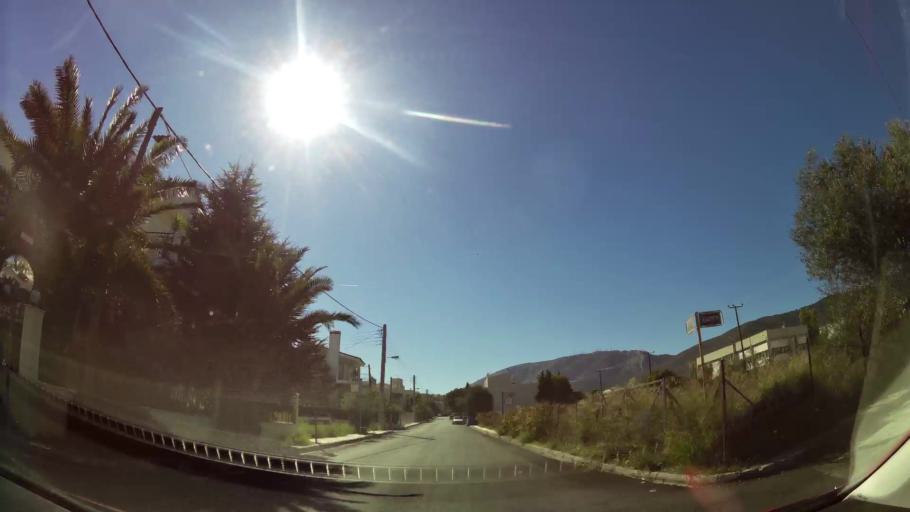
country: GR
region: Attica
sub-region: Nomarchia Anatolikis Attikis
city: Leondarion
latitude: 37.9915
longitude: 23.8594
